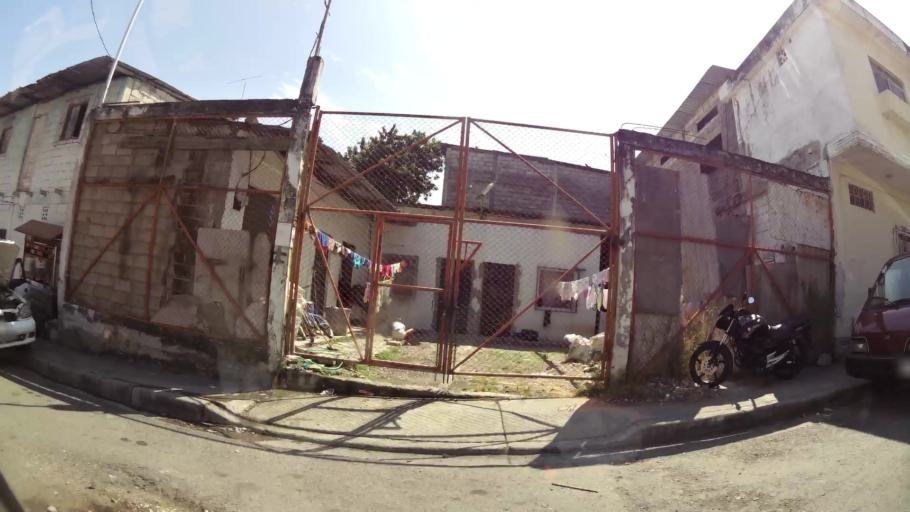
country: EC
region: Guayas
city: Guayaquil
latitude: -2.1312
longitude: -79.9202
